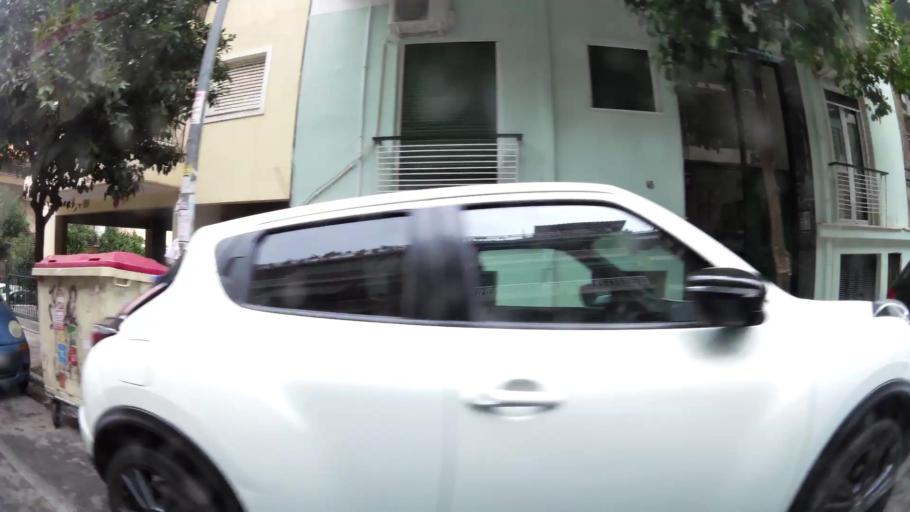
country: GR
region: Attica
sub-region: Nomarchia Athinas
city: Vyronas
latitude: 37.9623
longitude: 23.7490
